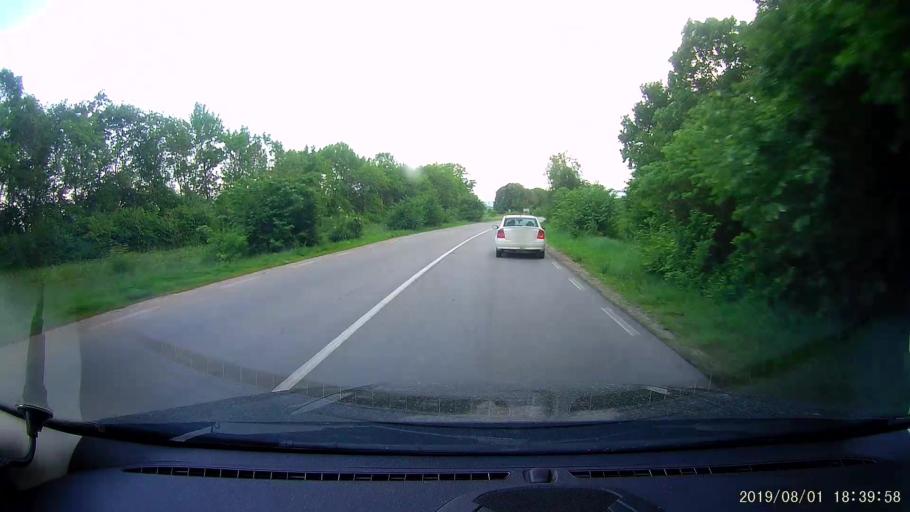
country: BG
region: Shumen
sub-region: Obshtina Khitrino
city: Gara Khitrino
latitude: 43.3751
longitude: 26.9199
